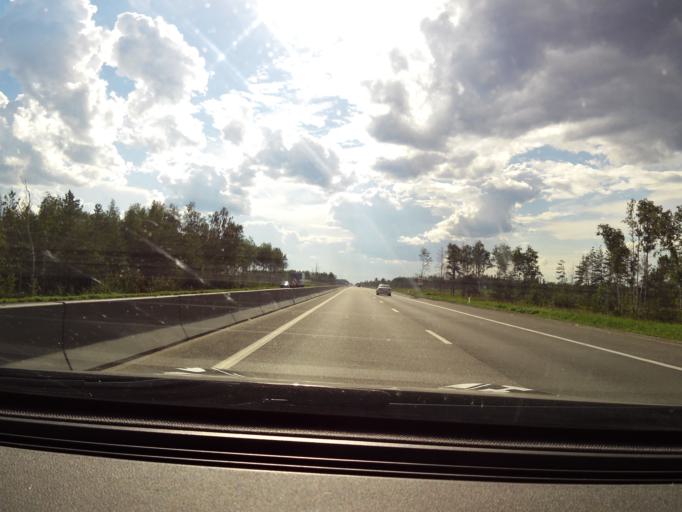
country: RU
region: Nizjnij Novgorod
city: Dzerzhinsk
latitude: 56.3009
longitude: 43.5371
